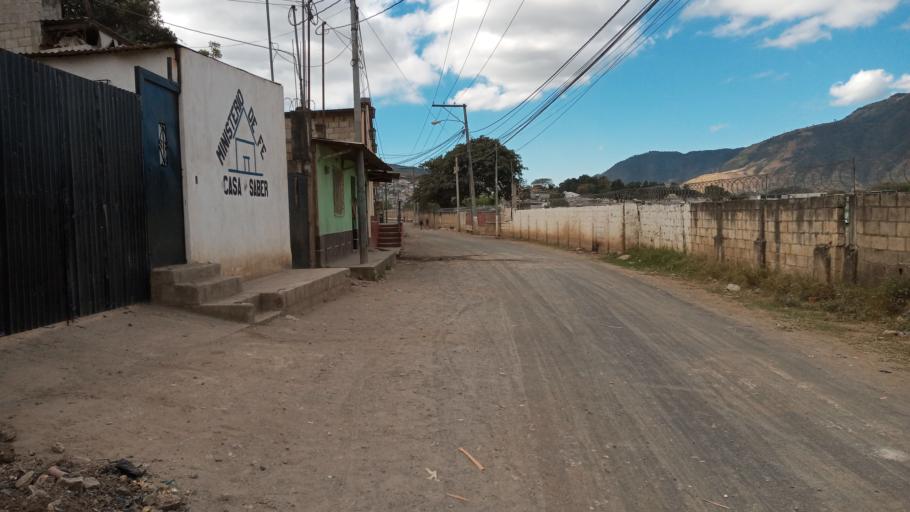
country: GT
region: Guatemala
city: Amatitlan
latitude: 14.4757
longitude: -90.6176
